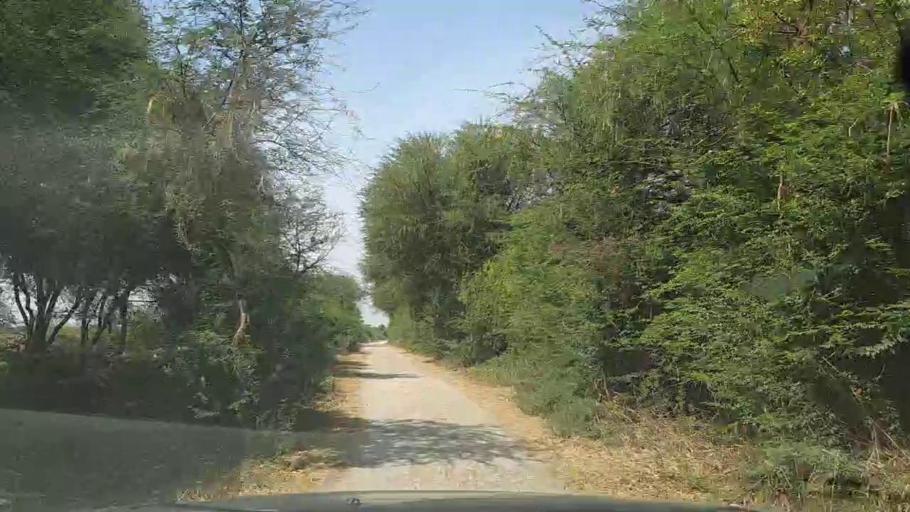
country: PK
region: Sindh
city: Mirpur Batoro
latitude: 24.6524
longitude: 68.1698
